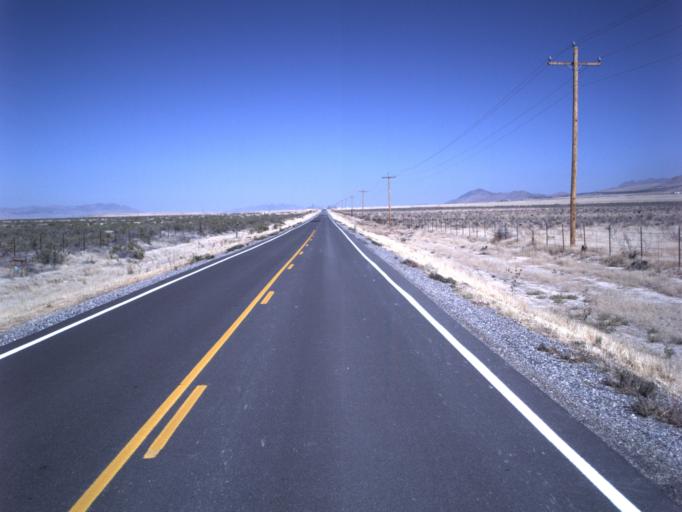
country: US
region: Utah
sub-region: Tooele County
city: Grantsville
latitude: 40.3552
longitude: -112.7456
